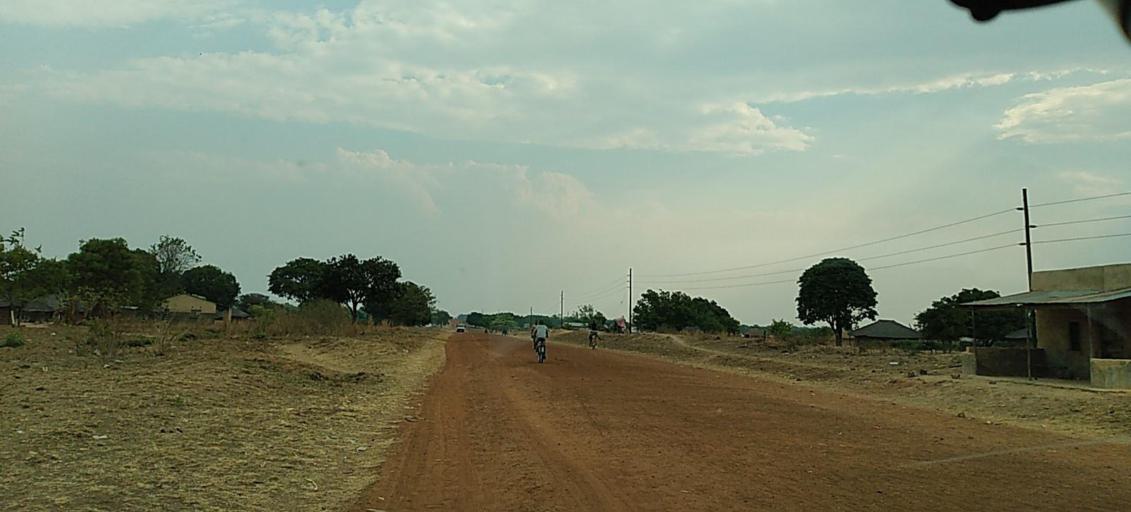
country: ZM
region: North-Western
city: Kabompo
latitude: -13.8626
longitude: 23.6715
